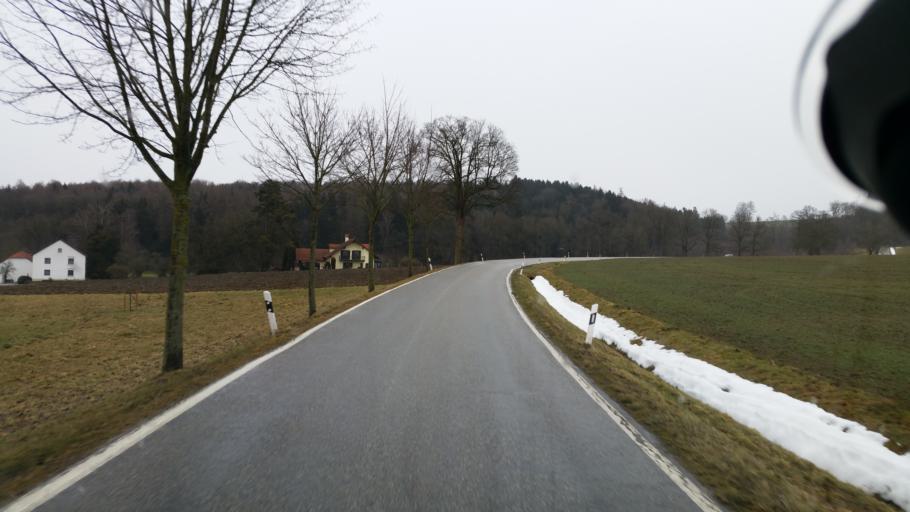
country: DE
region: Bavaria
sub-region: Lower Bavaria
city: Tiefenbach
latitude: 48.4815
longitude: 12.0949
